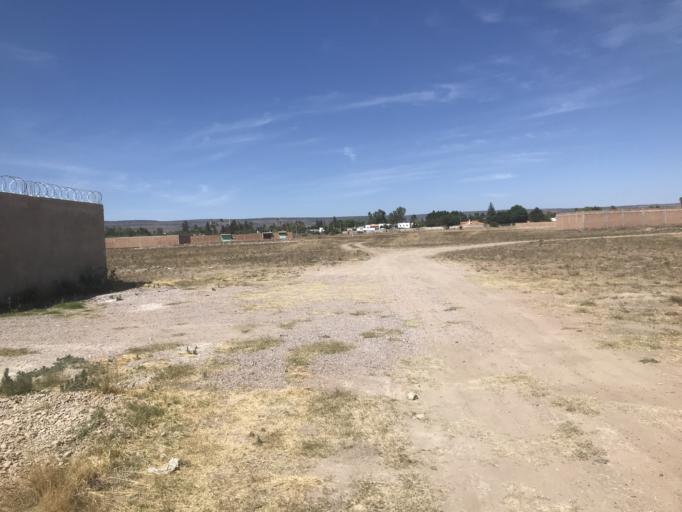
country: MX
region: Durango
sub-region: Durango
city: Sebastian Lerdo de Tejada
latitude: 23.9766
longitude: -104.6557
